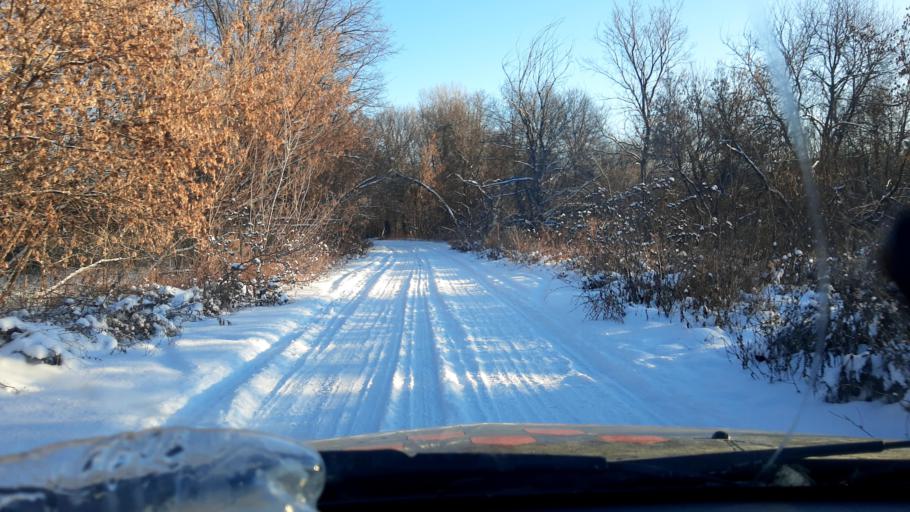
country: RU
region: Bashkortostan
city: Ufa
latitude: 54.6619
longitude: 55.9618
